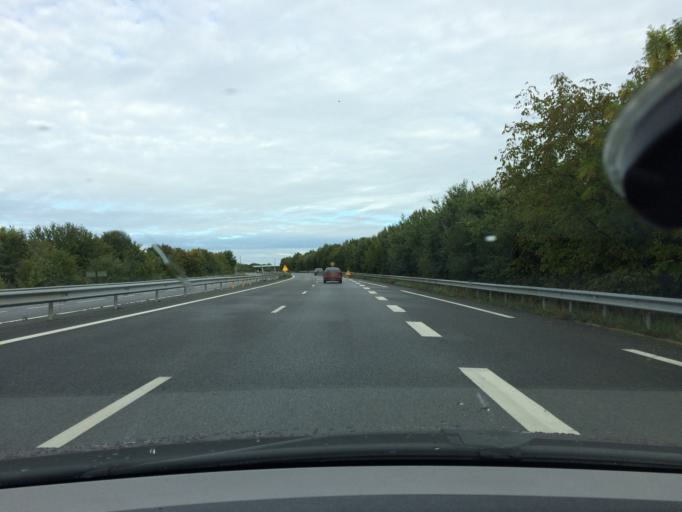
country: FR
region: Brittany
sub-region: Departement d'Ille-et-Vilaine
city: Janze
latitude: 47.9542
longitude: -1.5116
